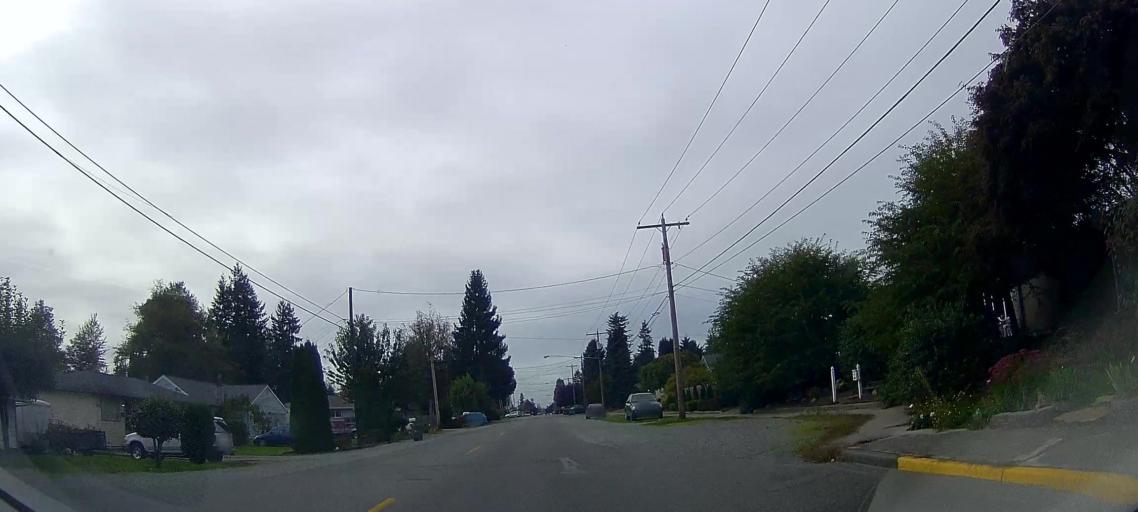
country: US
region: Washington
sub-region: Skagit County
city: Burlington
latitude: 48.4716
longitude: -122.3196
